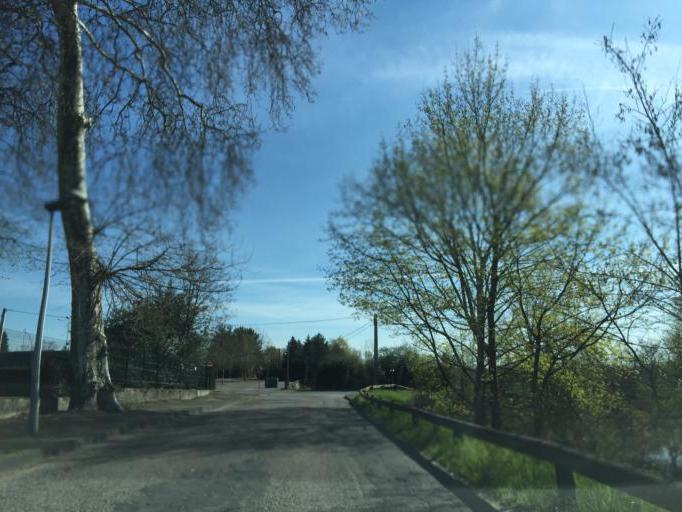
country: FR
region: Rhone-Alpes
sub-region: Departement de la Loire
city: Feurs
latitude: 45.7497
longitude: 4.2245
